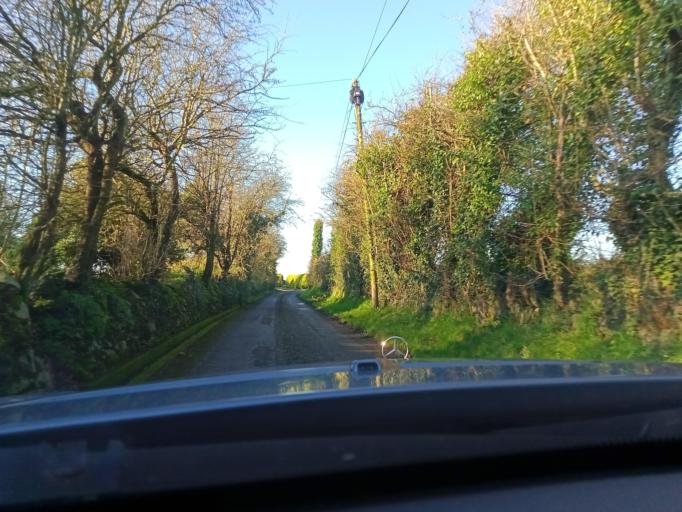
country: IE
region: Leinster
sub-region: Kilkenny
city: Mooncoin
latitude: 52.2934
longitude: -7.2071
